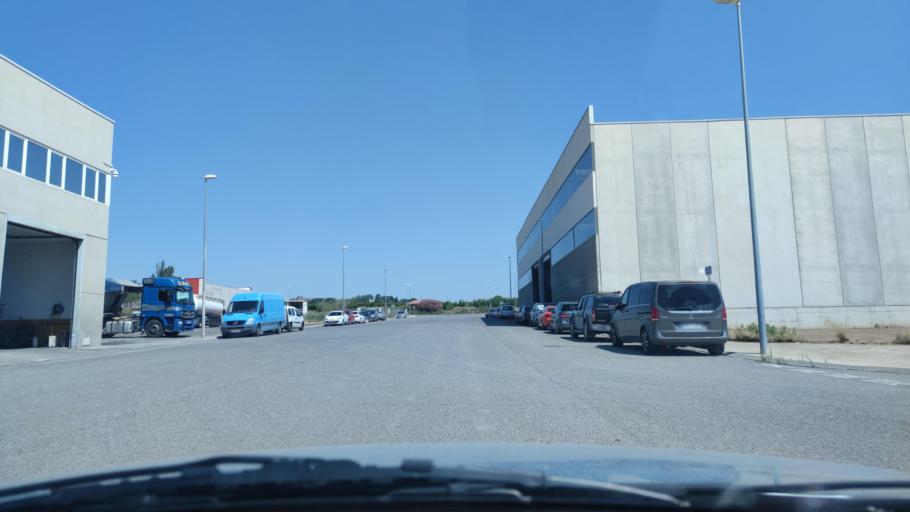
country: ES
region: Catalonia
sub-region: Provincia de Lleida
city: Torrefarrera
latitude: 41.6670
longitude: 0.5971
